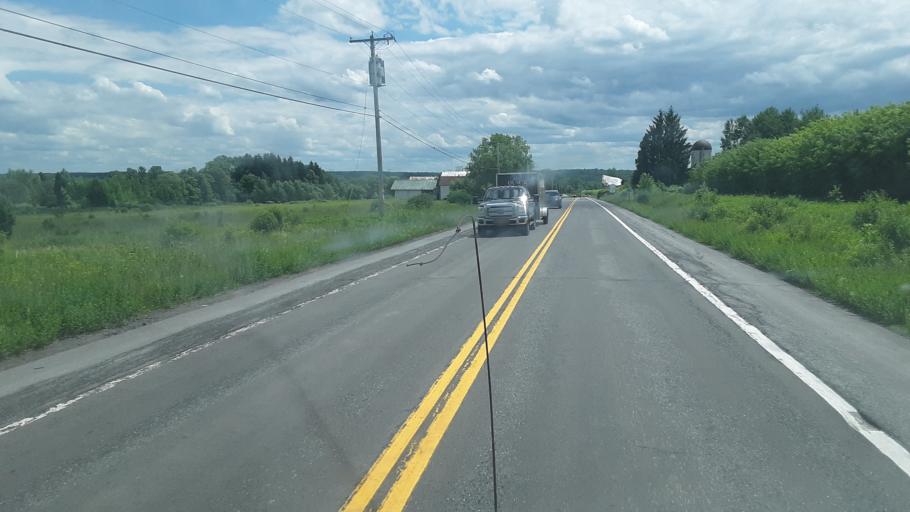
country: US
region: New York
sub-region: Oneida County
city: Rome
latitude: 43.3880
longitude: -75.4880
